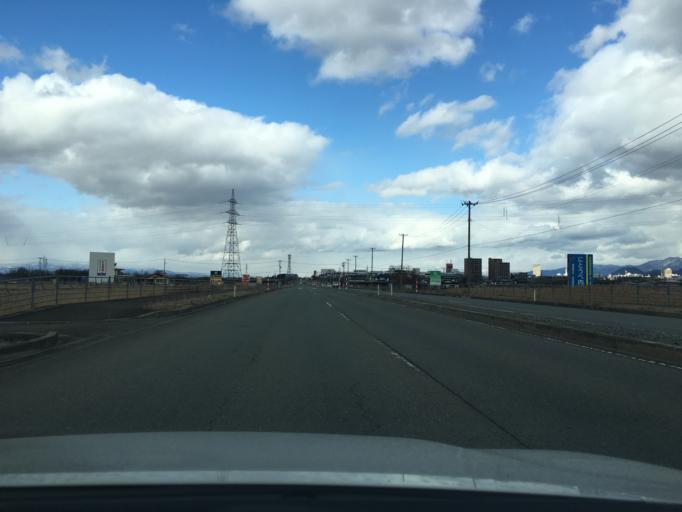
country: JP
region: Yamagata
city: Yamagata-shi
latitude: 38.2179
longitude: 140.3017
